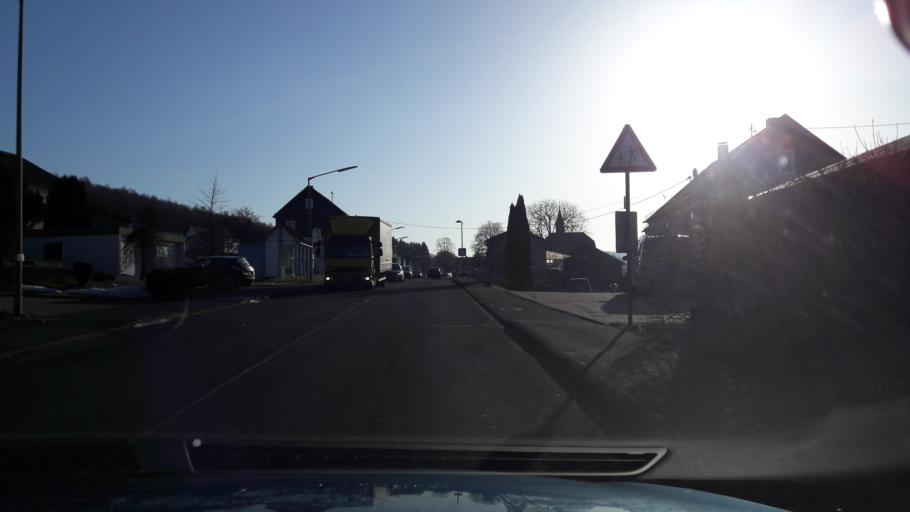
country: DE
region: North Rhine-Westphalia
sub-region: Regierungsbezirk Arnsberg
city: Burbach
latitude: 50.7690
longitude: 8.0847
